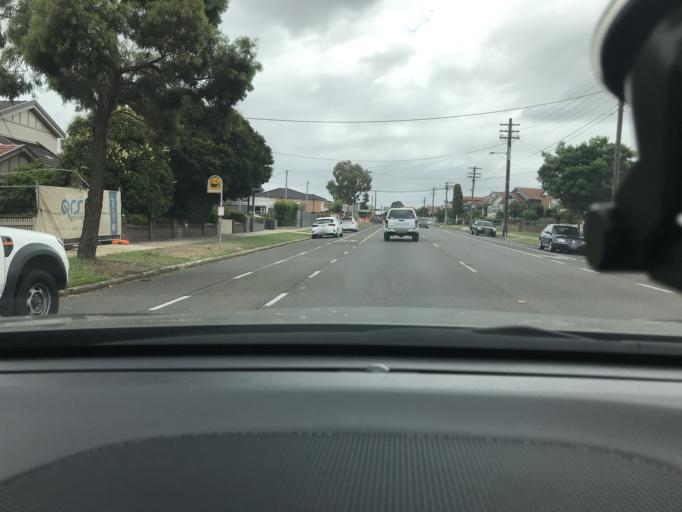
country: AU
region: New South Wales
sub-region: Canada Bay
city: Wareemba
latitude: -33.8609
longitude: 151.1307
